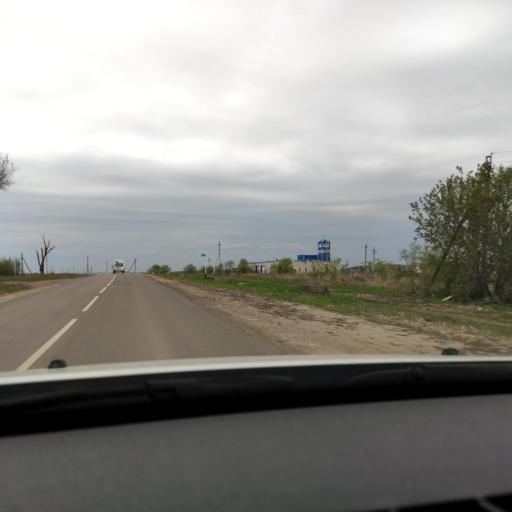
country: RU
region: Voronezj
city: Novovoronezh
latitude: 51.3474
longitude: 39.2877
